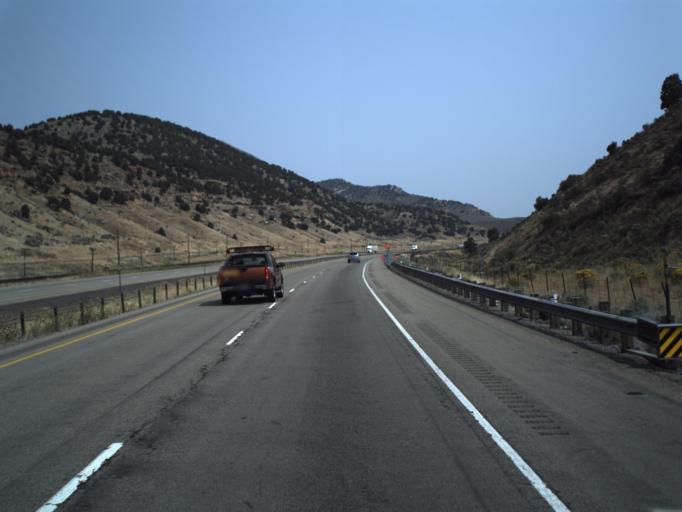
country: US
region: Utah
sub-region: Summit County
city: Coalville
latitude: 41.0373
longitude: -111.3296
